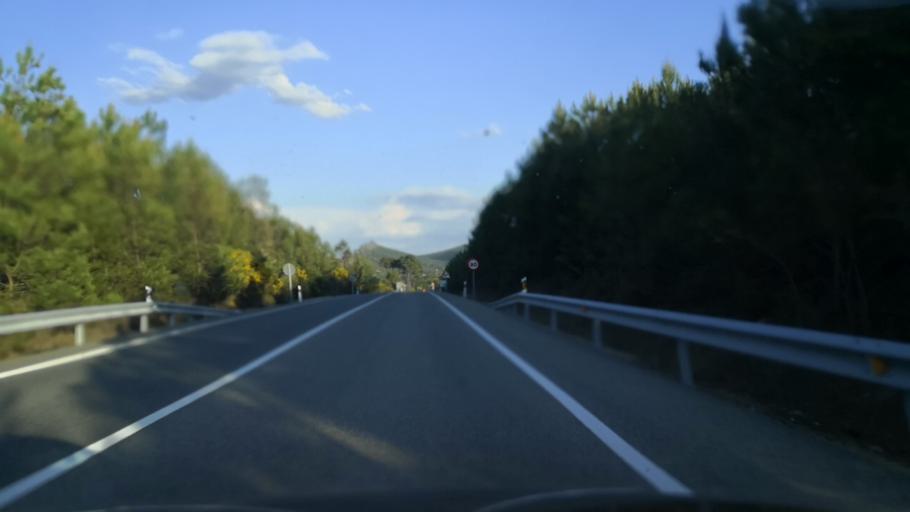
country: PT
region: Portalegre
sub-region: Portalegre
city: Sao Juliao
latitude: 39.3487
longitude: -7.3020
